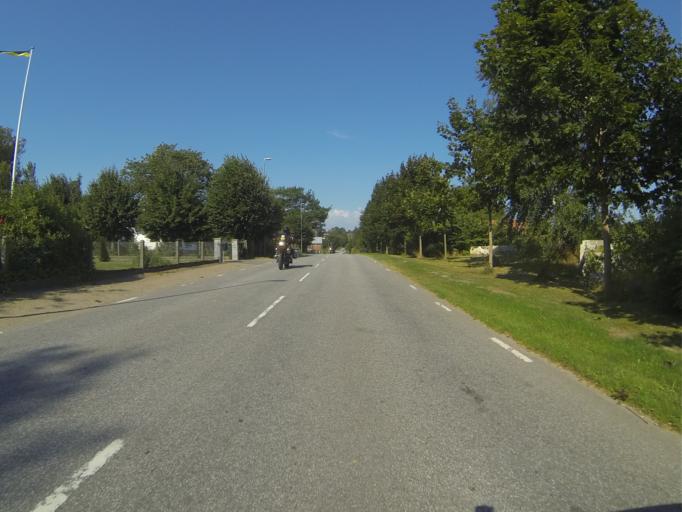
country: SE
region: Skane
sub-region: Hoors Kommun
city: Loberod
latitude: 55.7145
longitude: 13.5215
